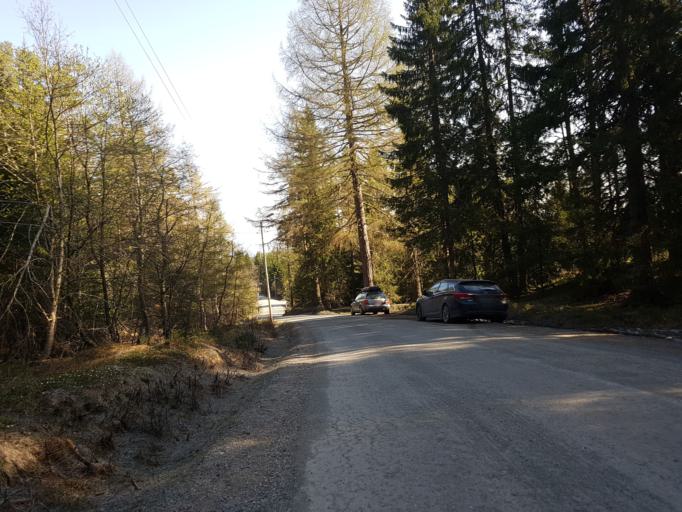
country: NO
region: Sor-Trondelag
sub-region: Trondheim
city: Trondheim
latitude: 63.4239
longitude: 10.3052
